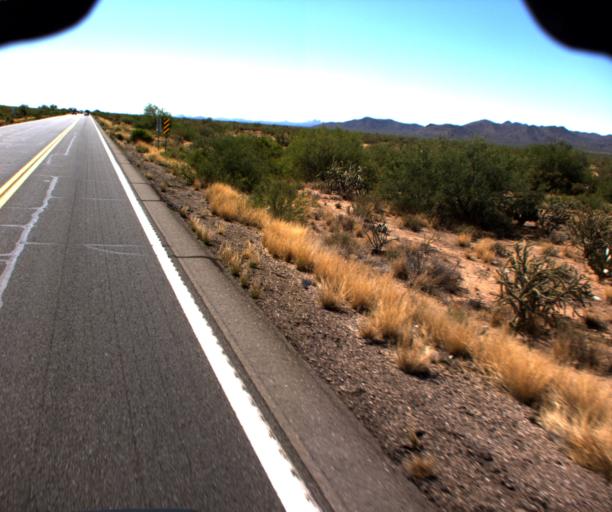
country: US
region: Arizona
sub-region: Yavapai County
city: Congress
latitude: 34.1381
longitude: -112.9717
